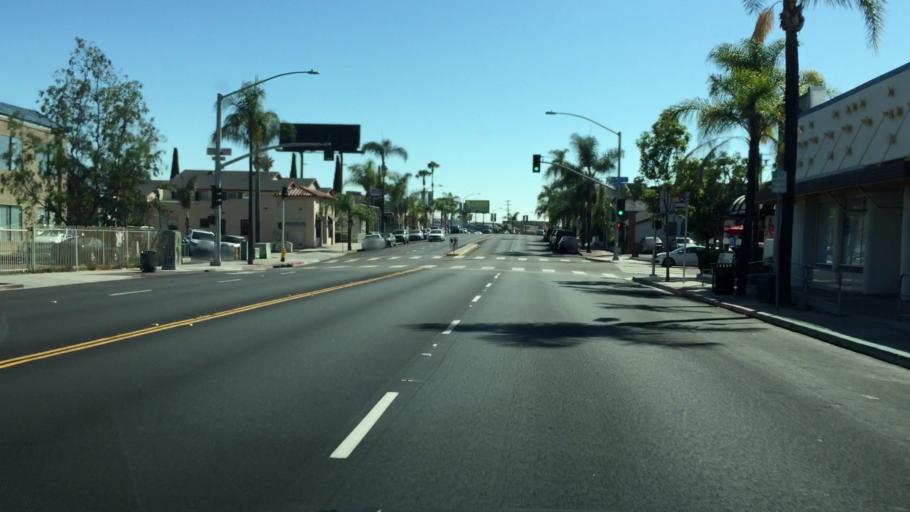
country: US
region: California
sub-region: San Diego County
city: Lemon Grove
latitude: 32.7600
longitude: -117.0701
